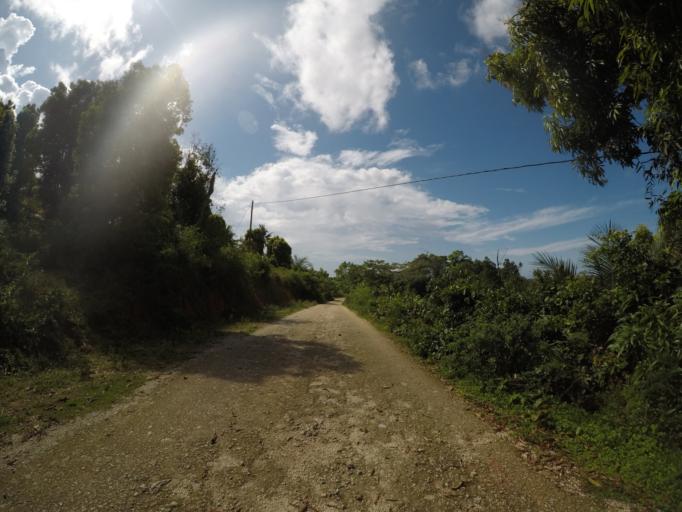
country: TZ
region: Pemba South
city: Mtambile
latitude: -5.3487
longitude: 39.6914
